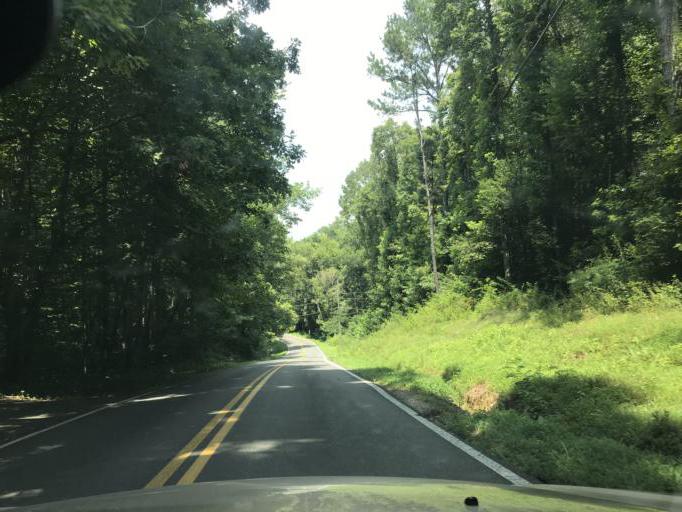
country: US
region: Georgia
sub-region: Dawson County
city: Dawsonville
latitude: 34.3316
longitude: -84.1781
